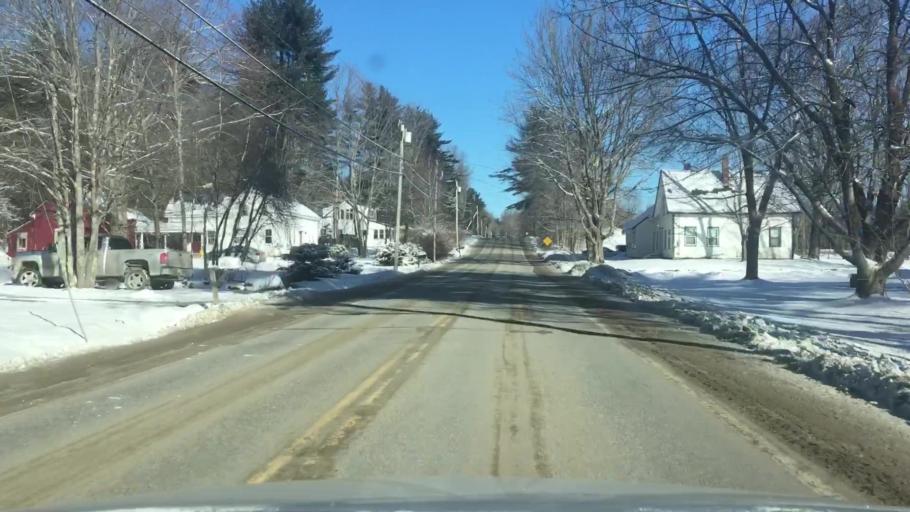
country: US
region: Maine
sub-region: Kennebec County
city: Readfield
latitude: 44.3909
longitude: -69.9656
